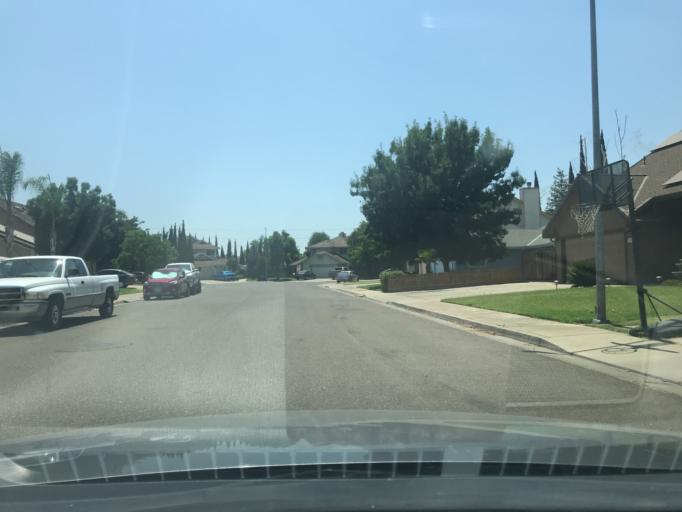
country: US
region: California
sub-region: Merced County
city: Atwater
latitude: 37.3695
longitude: -120.5940
